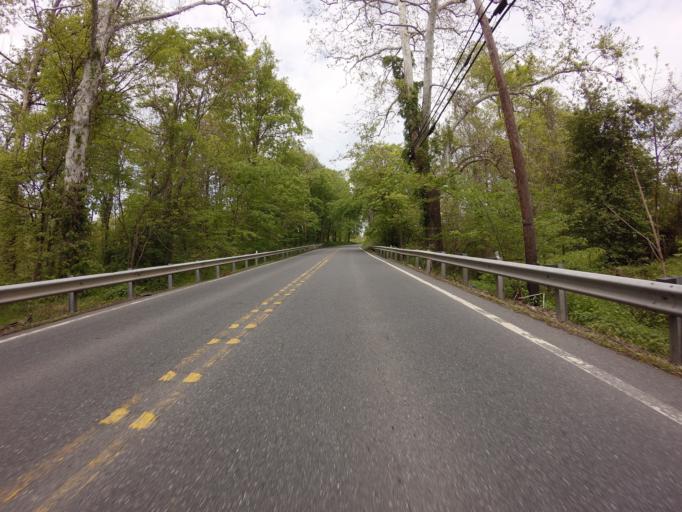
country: US
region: Maryland
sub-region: Frederick County
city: Urbana
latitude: 39.3181
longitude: -77.3341
